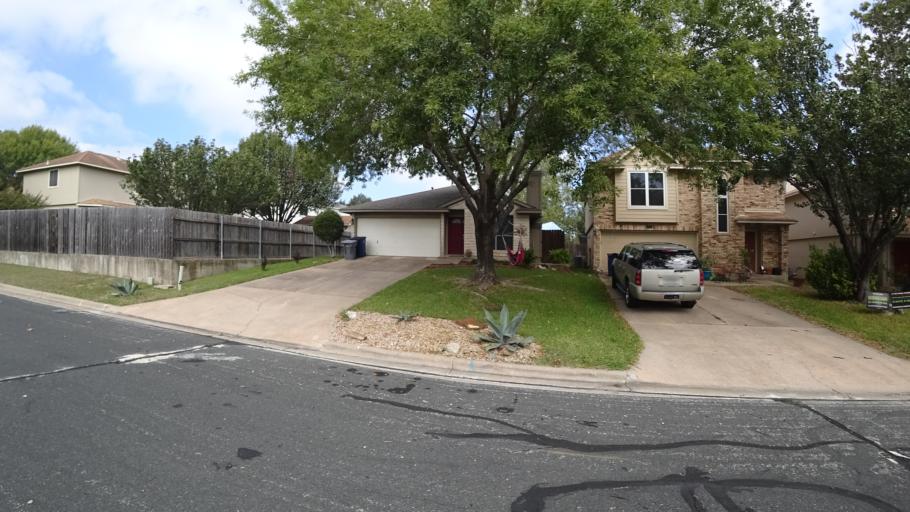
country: US
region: Texas
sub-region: Travis County
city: Shady Hollow
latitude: 30.1944
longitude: -97.8341
